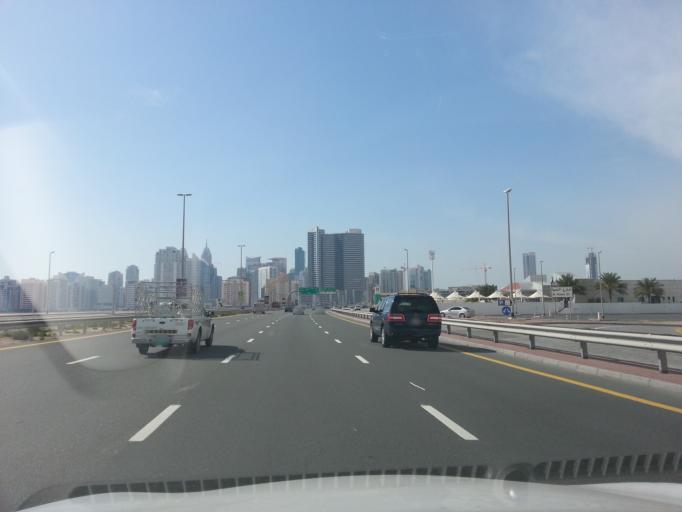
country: AE
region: Dubai
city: Dubai
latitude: 25.0903
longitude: 55.1883
